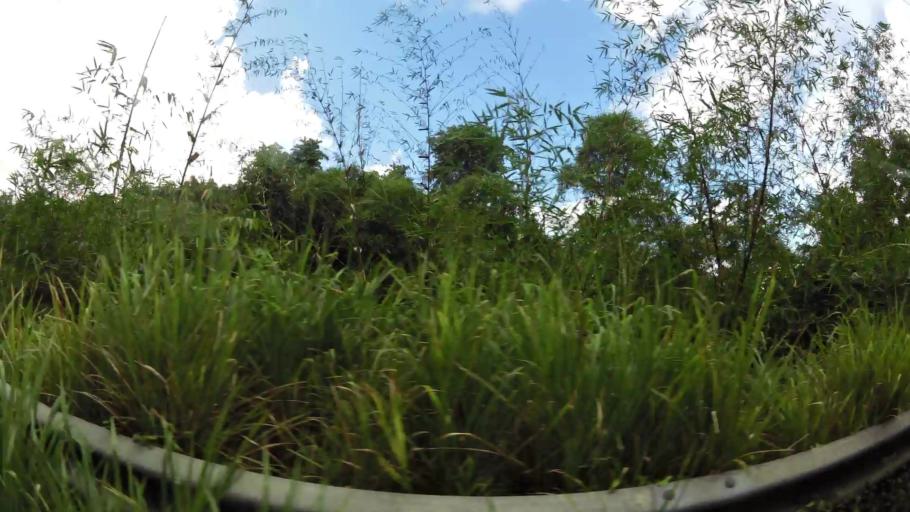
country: MQ
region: Martinique
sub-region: Martinique
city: Les Trois-Ilets
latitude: 14.5156
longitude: -61.0749
